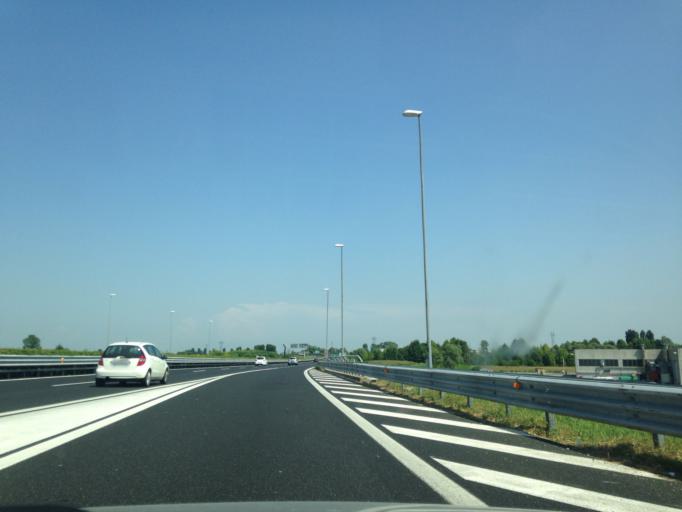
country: IT
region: Friuli Venezia Giulia
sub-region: Provincia di Pordenone
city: Tamai
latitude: 45.9413
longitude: 12.5433
